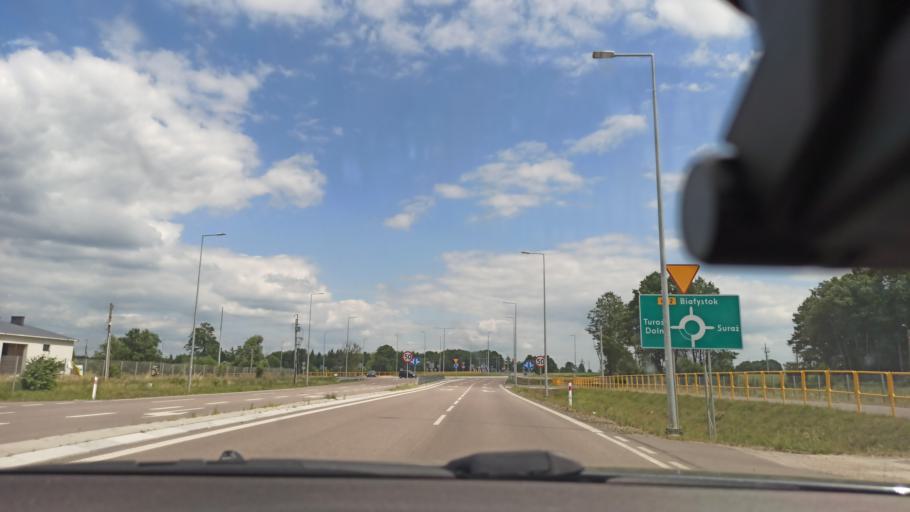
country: PL
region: Podlasie
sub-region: Powiat bialostocki
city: Turosn Koscielna
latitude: 53.0166
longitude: 22.9994
